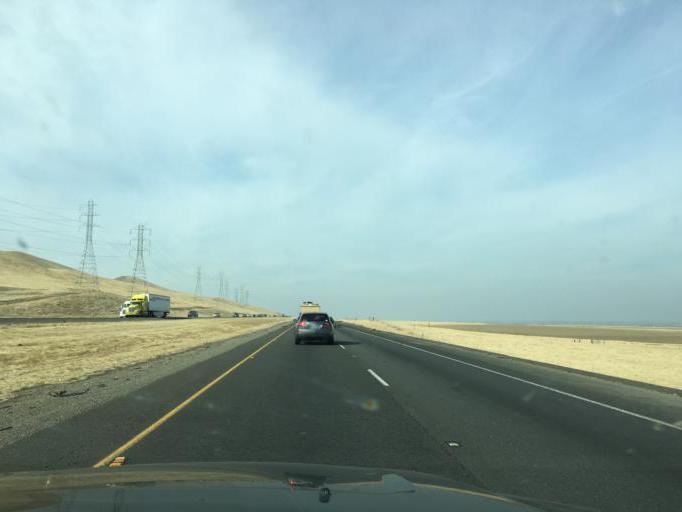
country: US
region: California
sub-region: Merced County
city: South Dos Palos
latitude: 36.8939
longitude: -120.8047
